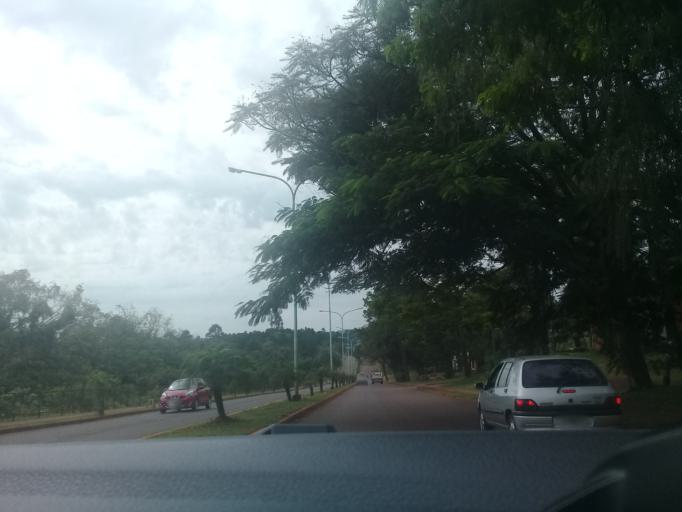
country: AR
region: Misiones
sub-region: Departamento de Obera
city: Obera
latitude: -27.4887
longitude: -55.1456
